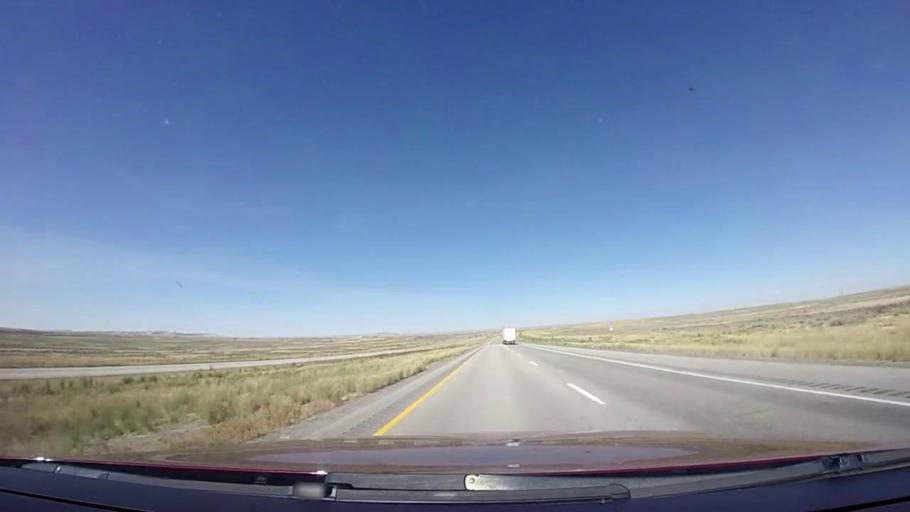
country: US
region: Wyoming
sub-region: Sweetwater County
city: Rock Springs
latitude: 41.6322
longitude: -108.3564
